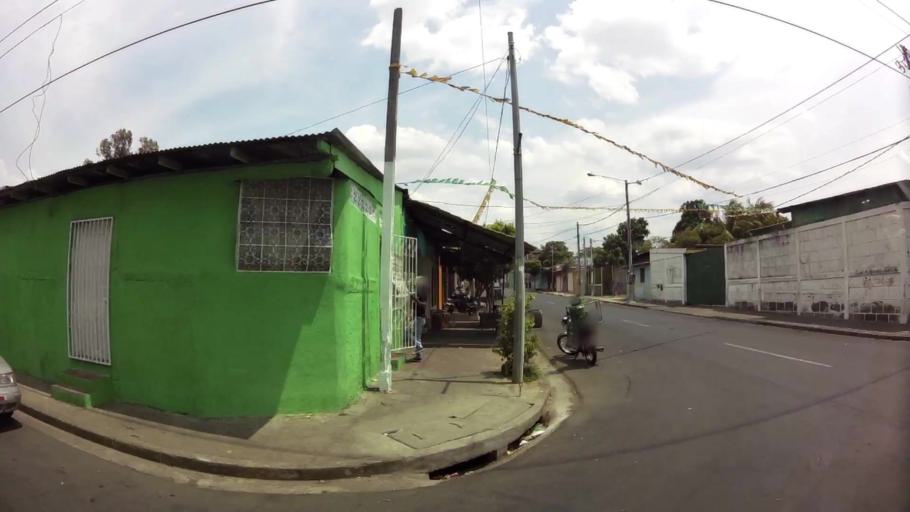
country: NI
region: Managua
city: Managua
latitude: 12.1496
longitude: -86.2889
